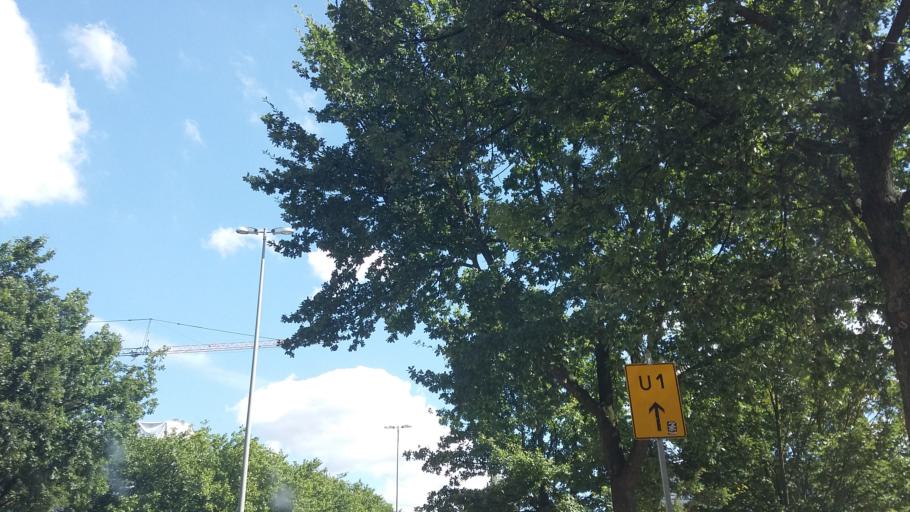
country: DE
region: Hamburg
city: St. Pauli
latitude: 53.5636
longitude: 9.9595
